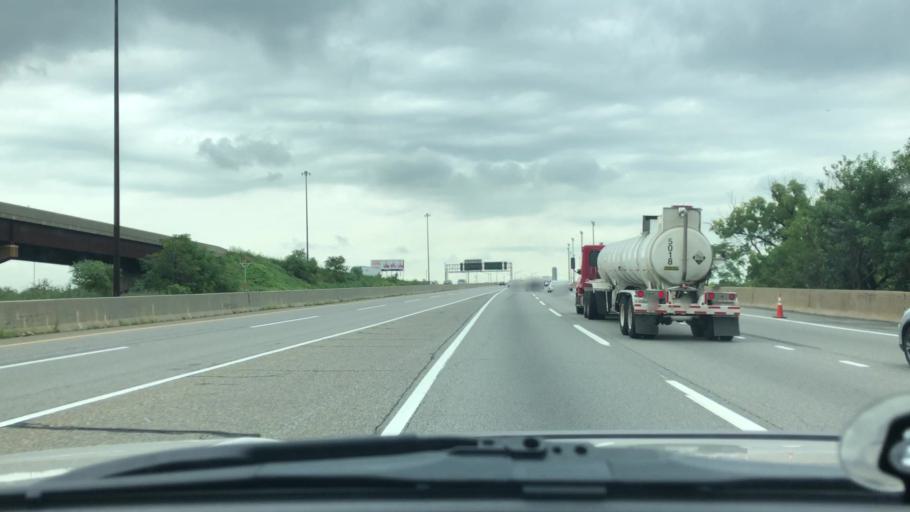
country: US
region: New Jersey
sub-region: Hudson County
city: Harrison
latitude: 40.7214
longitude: -74.1337
